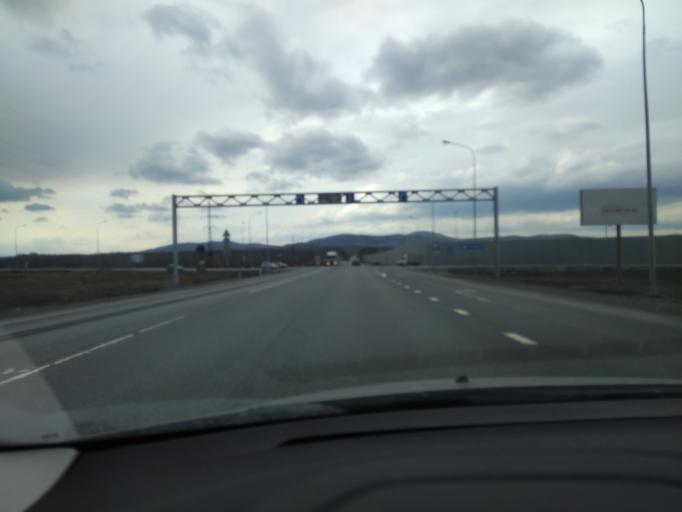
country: RU
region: Chelyabinsk
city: Miass
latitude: 54.9442
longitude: 60.0527
